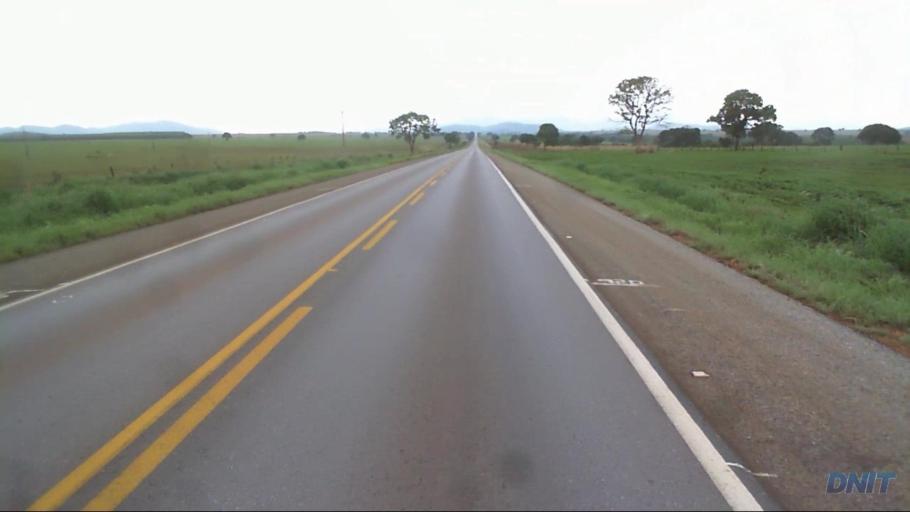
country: BR
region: Goias
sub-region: Barro Alto
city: Barro Alto
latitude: -14.8144
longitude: -49.0422
